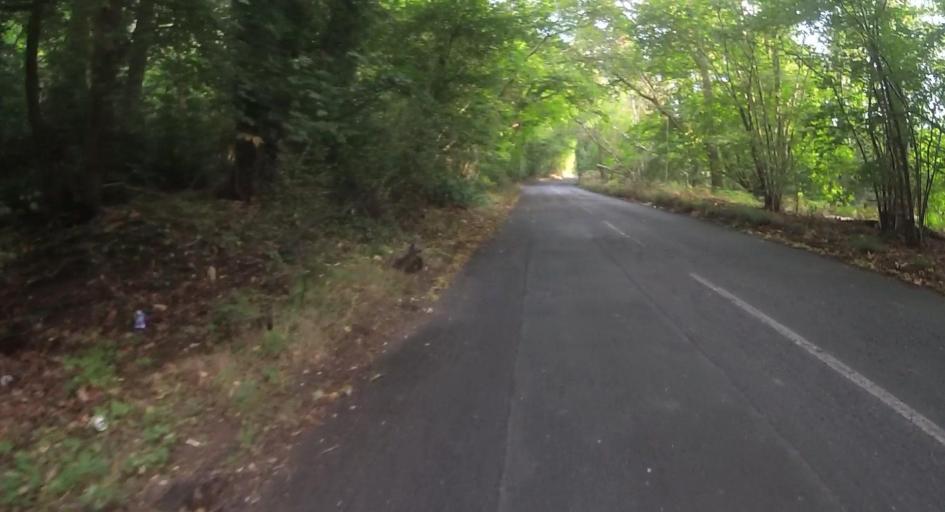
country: GB
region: England
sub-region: Hampshire
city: Tadley
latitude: 51.3785
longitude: -1.1342
